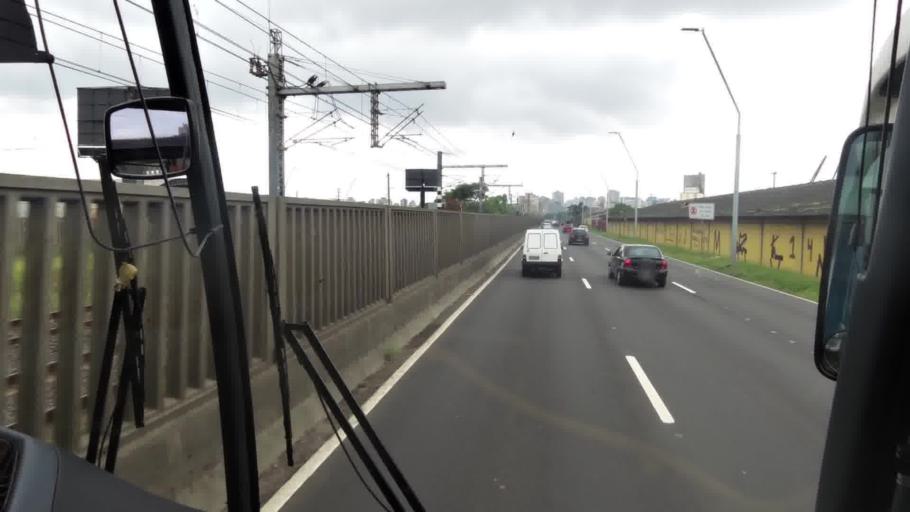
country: BR
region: Rio Grande do Sul
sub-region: Porto Alegre
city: Porto Alegre
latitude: -30.0134
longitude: -51.2131
